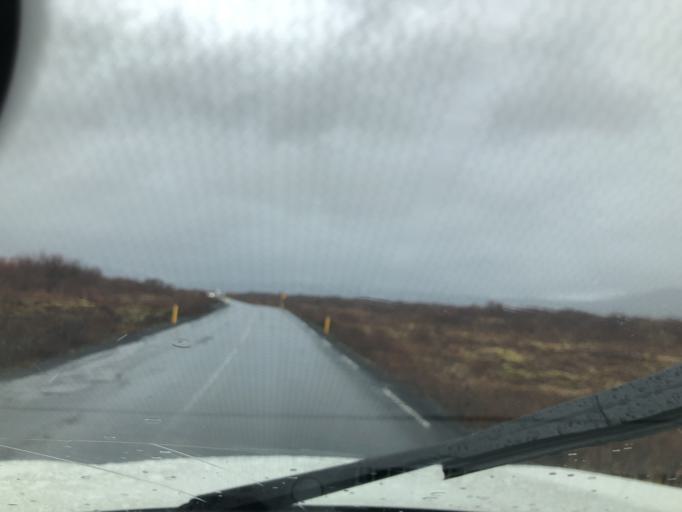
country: IS
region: South
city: Hveragerdi
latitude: 64.2642
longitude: -21.0549
